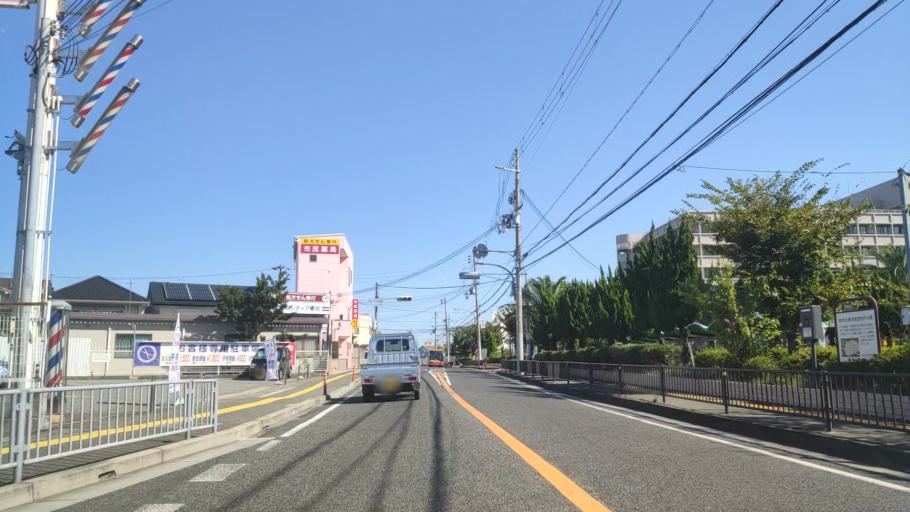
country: JP
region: Hyogo
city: Akashi
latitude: 34.6562
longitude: 134.9890
